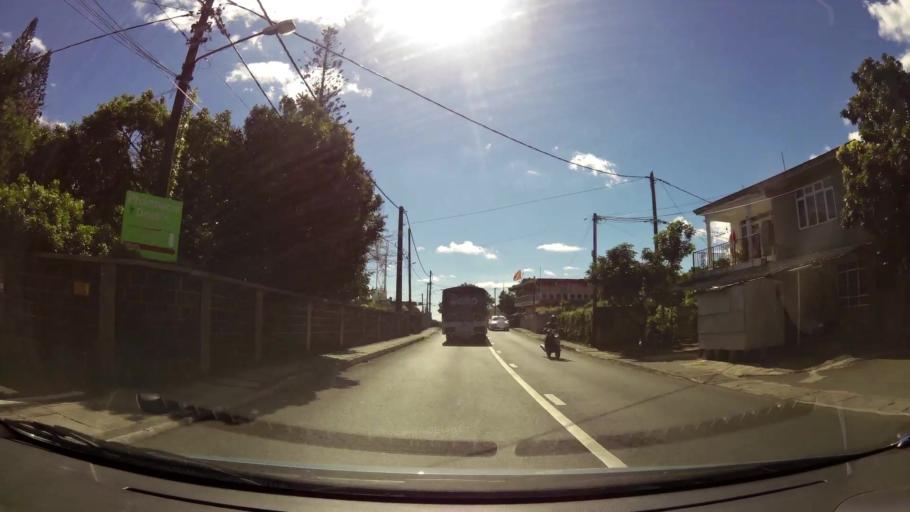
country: MU
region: Plaines Wilhems
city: Vacoas
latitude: -20.2890
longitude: 57.4816
